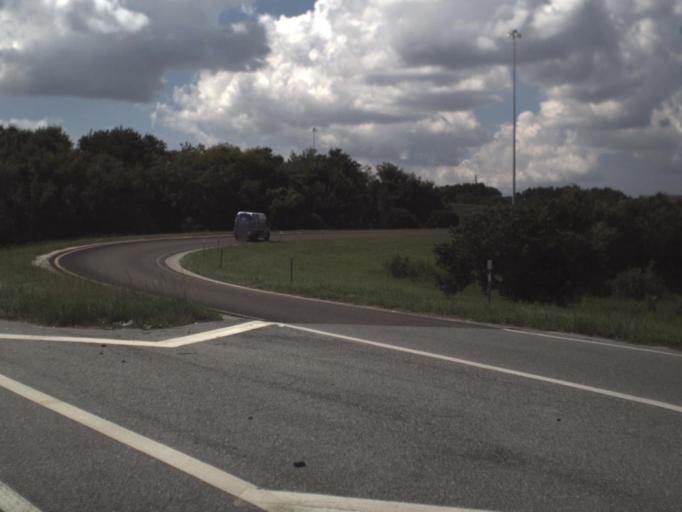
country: US
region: Florida
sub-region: Sarasota County
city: Fruitville
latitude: 27.3386
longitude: -82.4448
